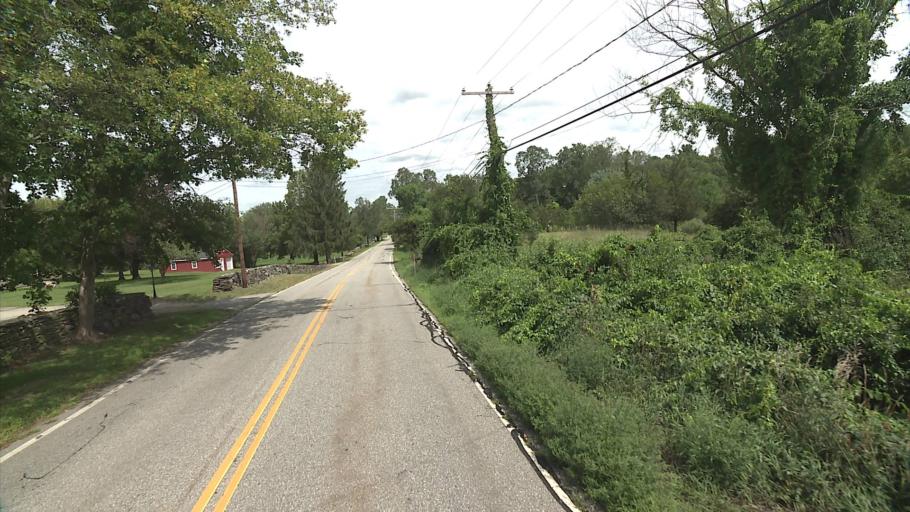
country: US
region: Connecticut
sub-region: Windham County
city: Thompson
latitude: 41.9304
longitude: -71.8672
